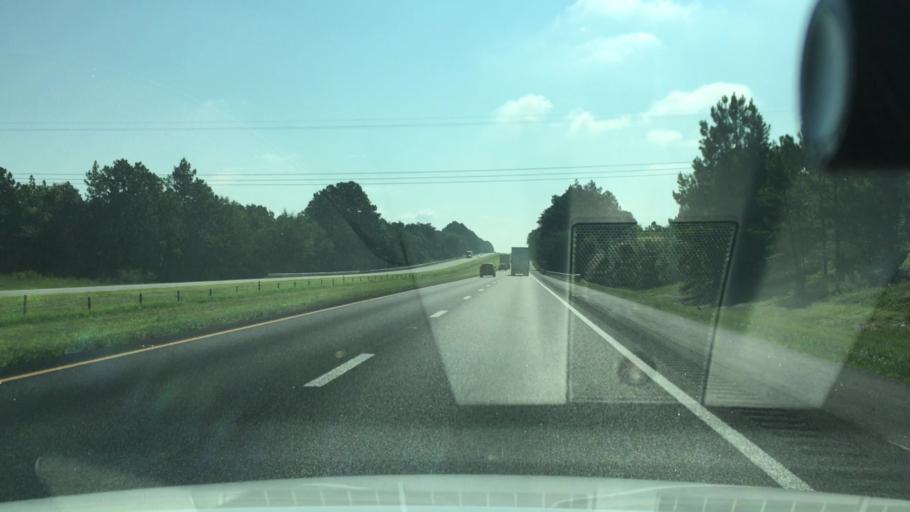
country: US
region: South Carolina
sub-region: Aiken County
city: Graniteville
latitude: 33.6341
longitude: -81.7773
